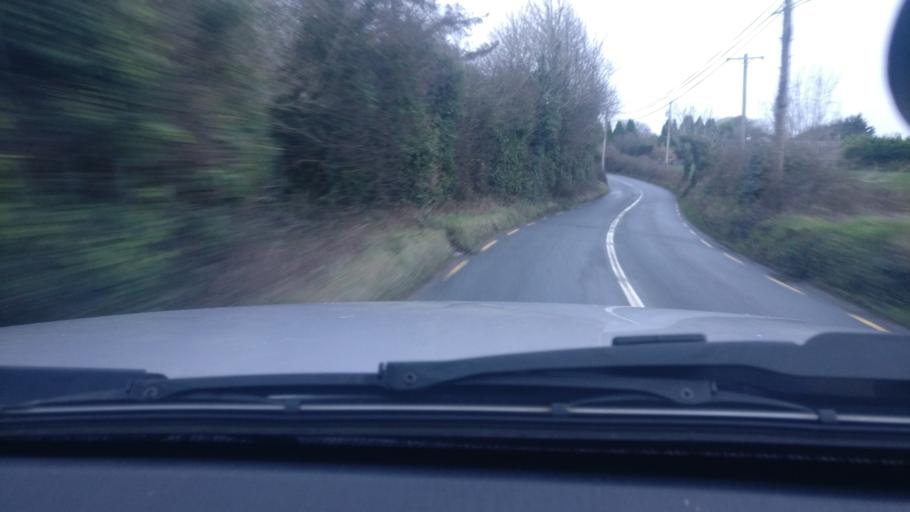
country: IE
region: Connaught
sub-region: County Galway
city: Loughrea
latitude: 53.1652
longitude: -8.5208
